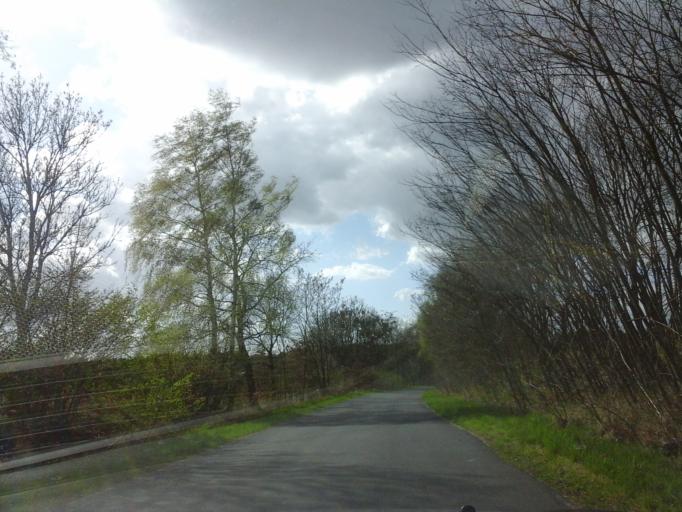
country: PL
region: West Pomeranian Voivodeship
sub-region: Powiat stargardzki
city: Suchan
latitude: 53.2240
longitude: 15.2860
